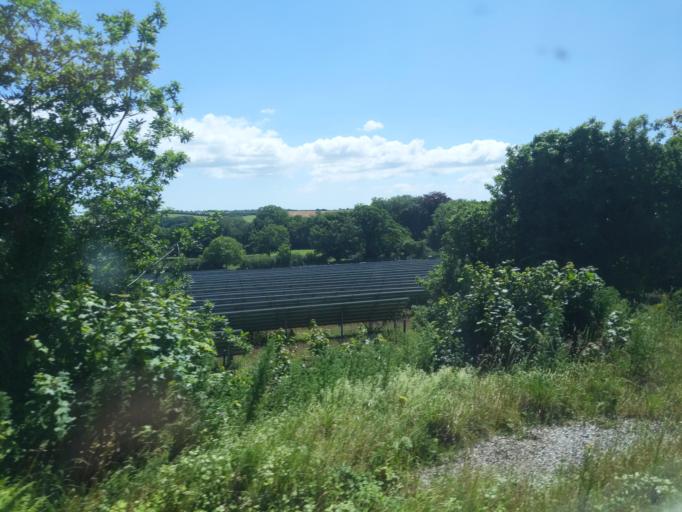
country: GB
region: England
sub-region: Cornwall
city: St Austell
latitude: 50.3380
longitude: -4.8326
